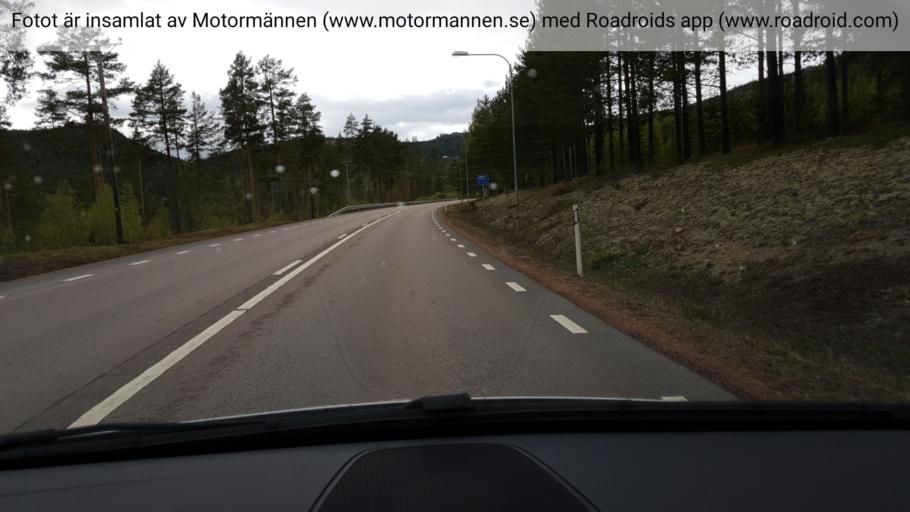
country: SE
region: Jaemtland
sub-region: Ragunda Kommun
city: Hammarstrand
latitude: 63.1454
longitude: 16.0988
